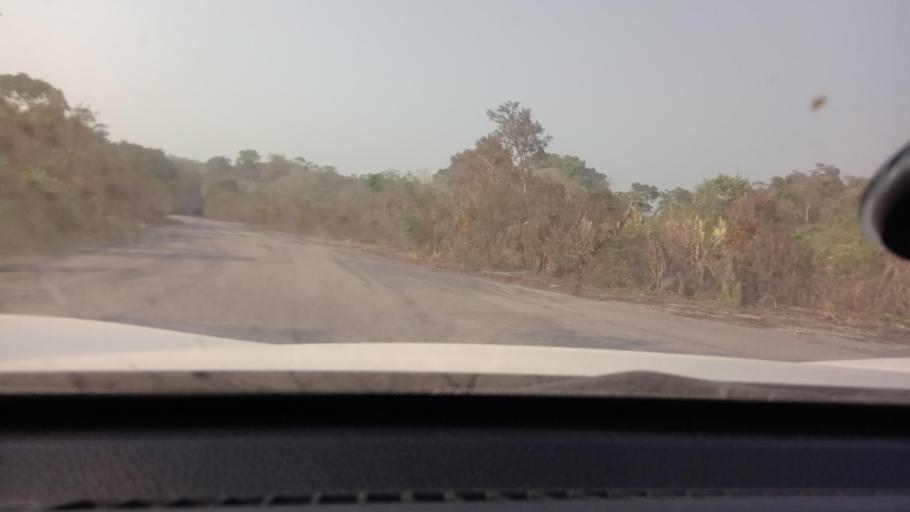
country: MX
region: Tabasco
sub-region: Huimanguillo
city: Francisco Rueda
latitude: 17.6699
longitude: -93.8670
